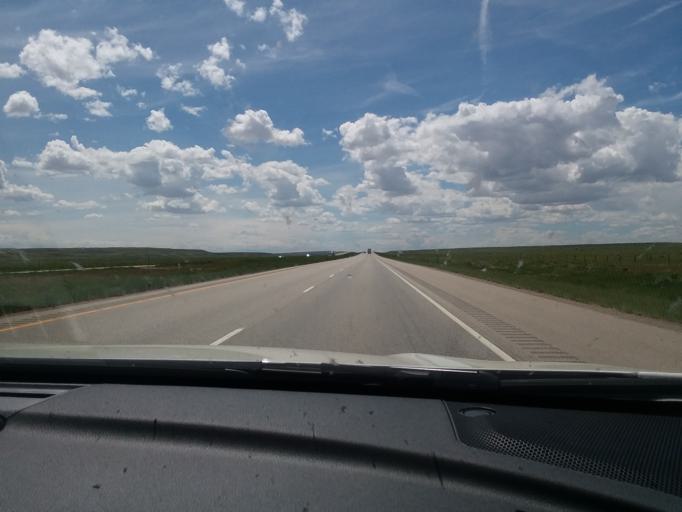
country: US
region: Wyoming
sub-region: Carbon County
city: Rawlins
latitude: 41.6628
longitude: -108.0528
